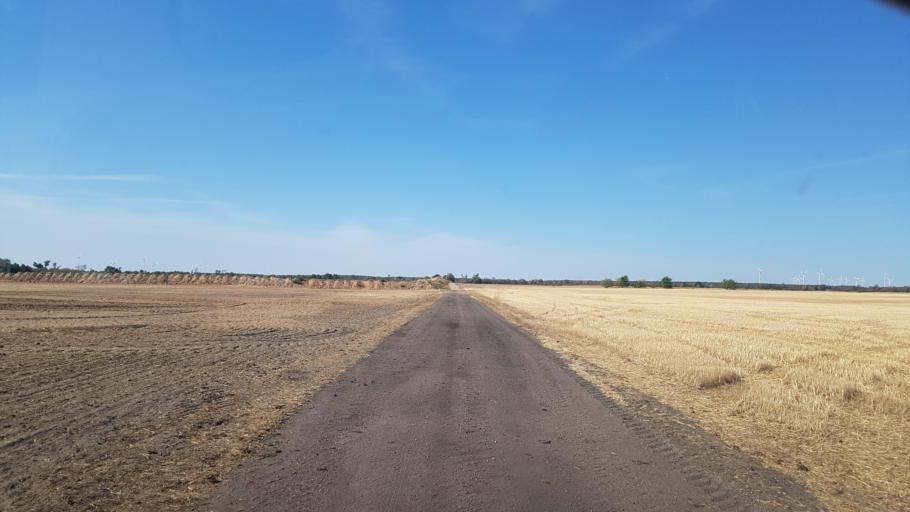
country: DE
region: Brandenburg
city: Muhlberg
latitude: 51.4164
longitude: 13.2866
